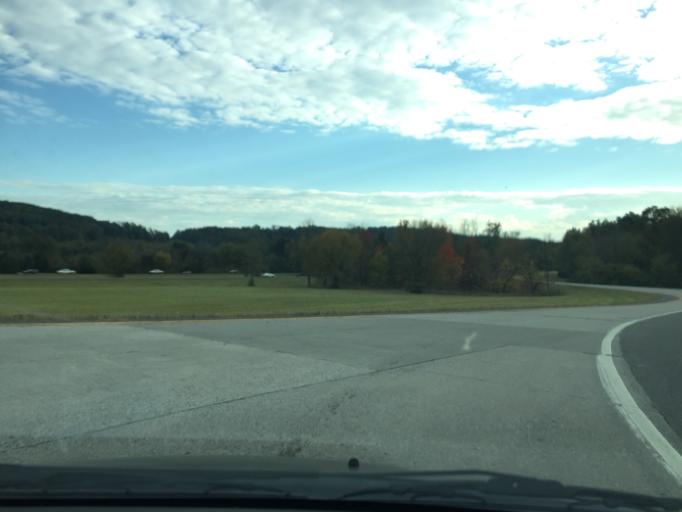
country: US
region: Tennessee
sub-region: Monroe County
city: Sweetwater
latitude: 35.6238
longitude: -84.4934
